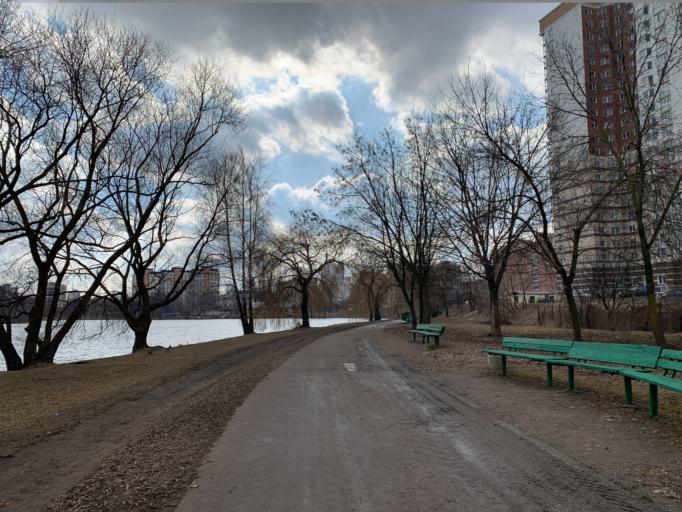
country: BY
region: Minsk
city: Minsk
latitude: 53.8796
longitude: 27.5711
